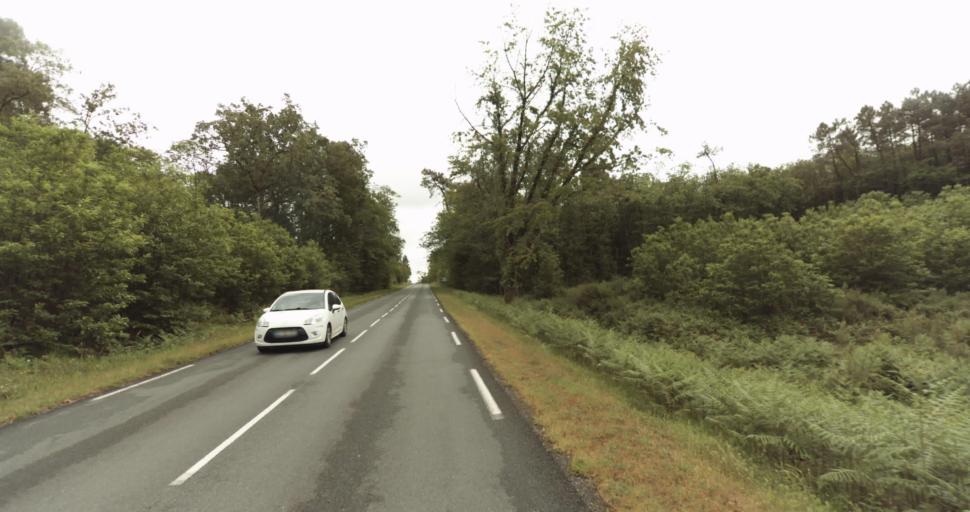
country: FR
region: Aquitaine
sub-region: Departement de la Dordogne
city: Belves
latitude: 44.6733
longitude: 0.9975
